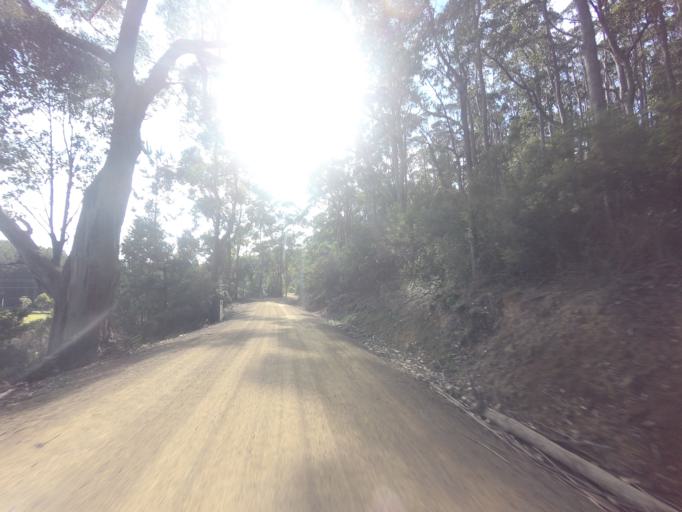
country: AU
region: Tasmania
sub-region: Clarence
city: Sandford
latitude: -43.1822
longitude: 147.7716
